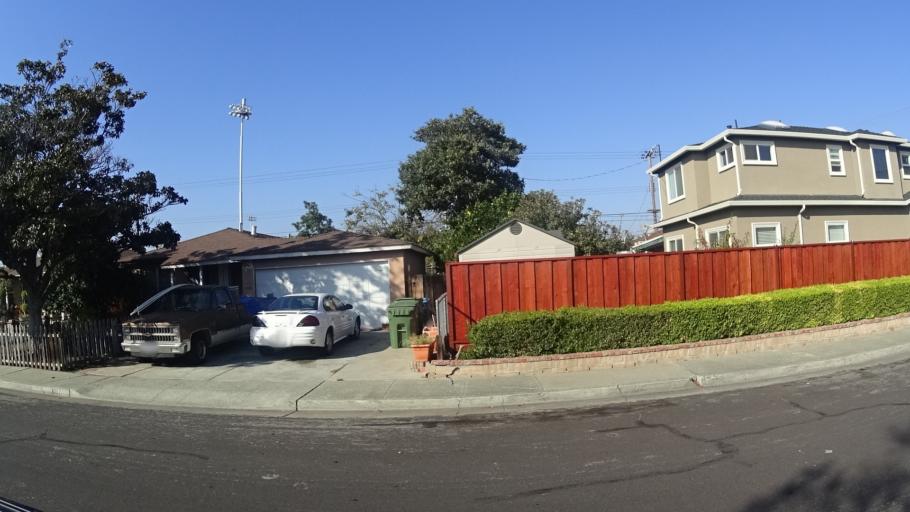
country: US
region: California
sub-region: Santa Clara County
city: Santa Clara
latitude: 37.3643
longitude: -121.9822
